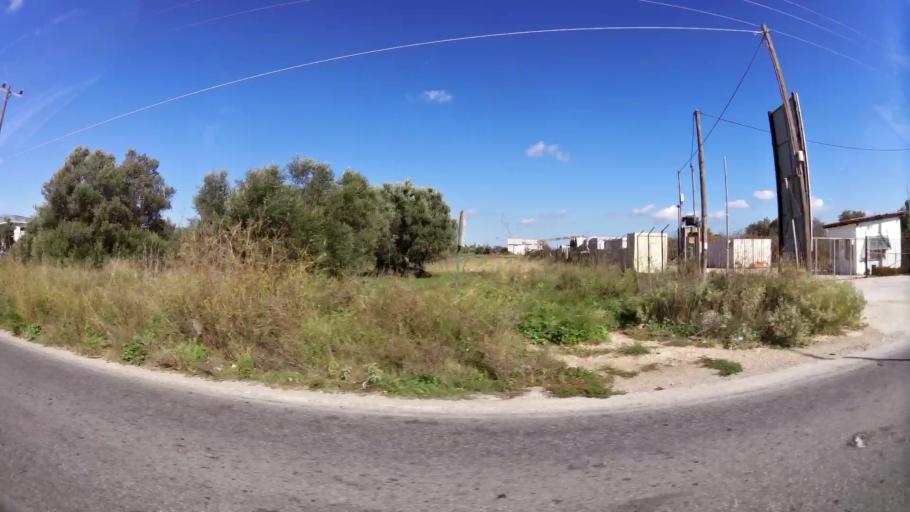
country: GR
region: Attica
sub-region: Nomarchia Anatolikis Attikis
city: Markopoulo
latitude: 37.8872
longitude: 23.9039
